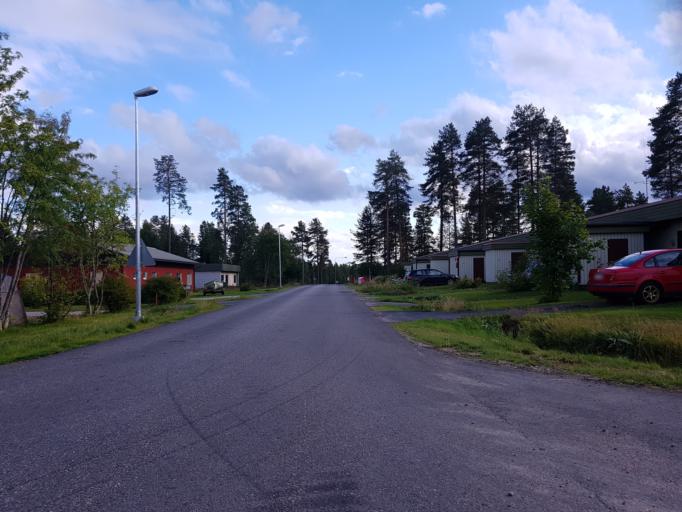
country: FI
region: Kainuu
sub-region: Kehys-Kainuu
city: Kuhmo
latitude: 64.1192
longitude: 29.5358
